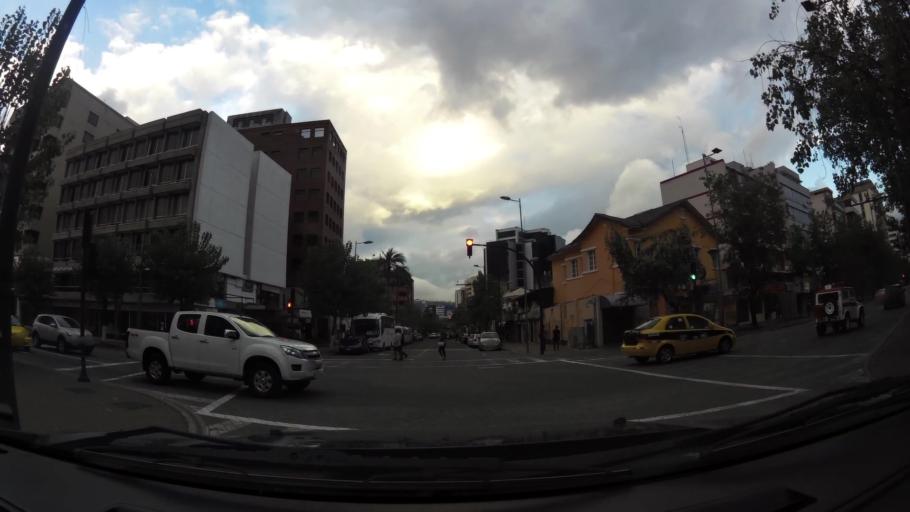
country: EC
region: Pichincha
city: Quito
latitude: -0.2024
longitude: -78.4941
